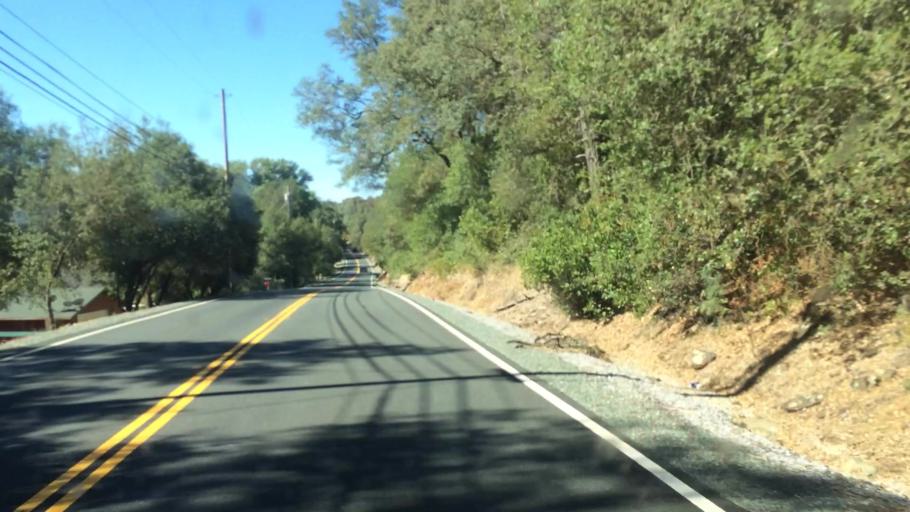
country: US
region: California
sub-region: Amador County
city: Plymouth
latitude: 38.5702
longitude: -120.8458
